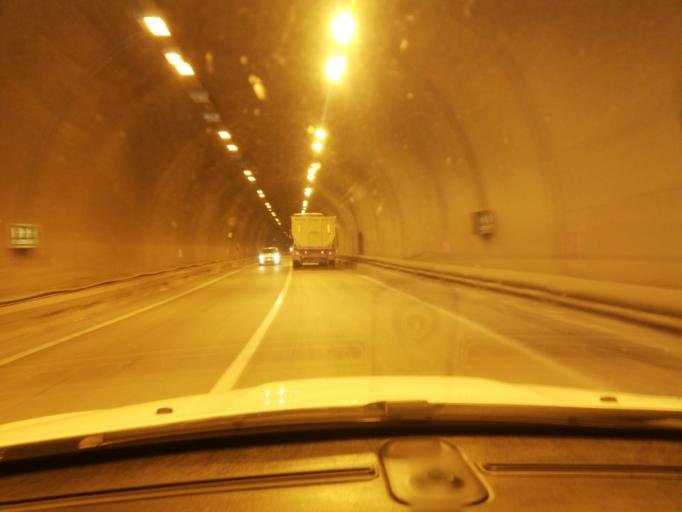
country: TR
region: Karabuk
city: Yenice
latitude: 41.1866
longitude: 32.4434
